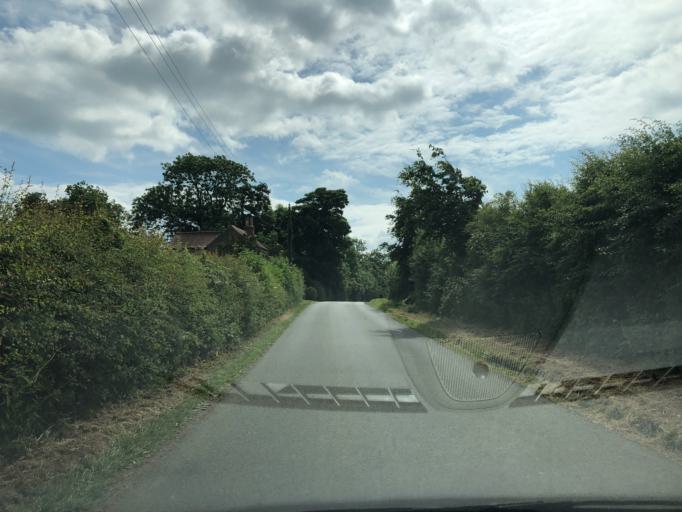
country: GB
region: England
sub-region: North Yorkshire
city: Strensall
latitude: 54.1447
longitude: -1.0056
